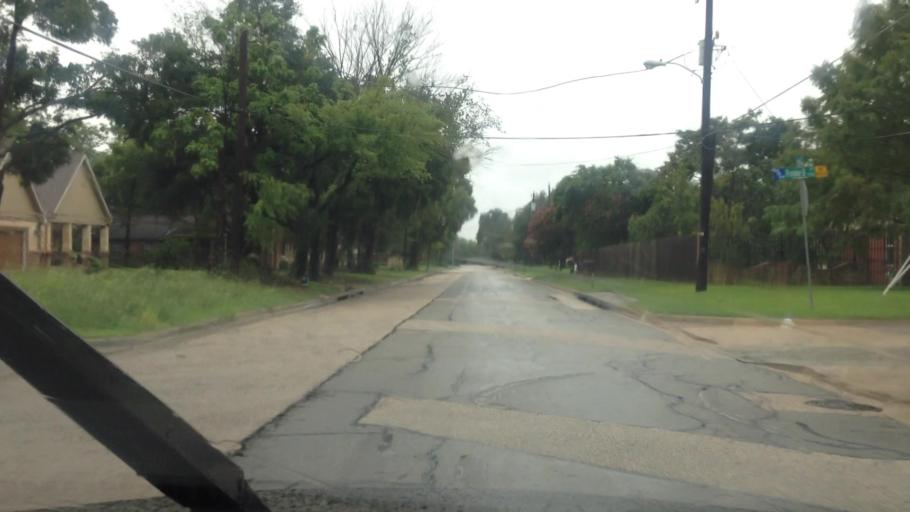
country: US
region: Texas
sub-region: Tarrant County
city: North Richland Hills
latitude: 32.8721
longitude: -97.2153
